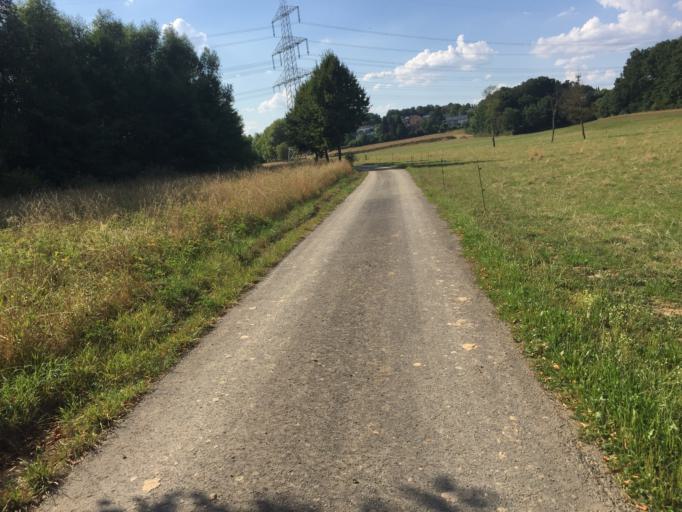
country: DE
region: Hesse
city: Allendorf an der Lahn
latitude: 50.5491
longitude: 8.6316
